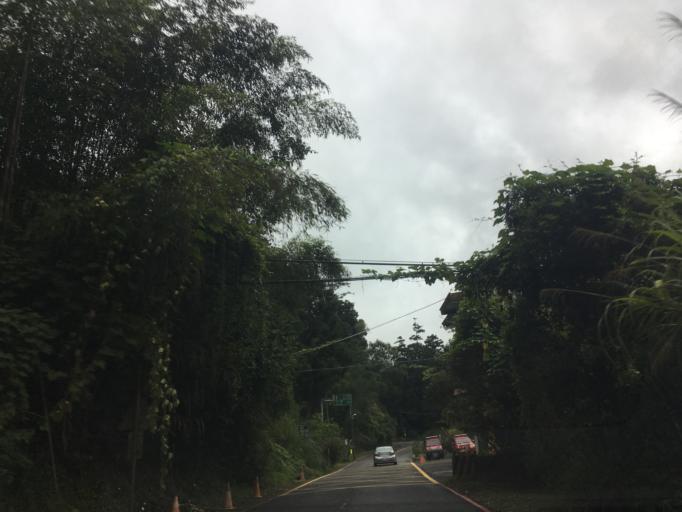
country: TW
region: Taiwan
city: Lugu
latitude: 23.5020
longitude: 120.6989
